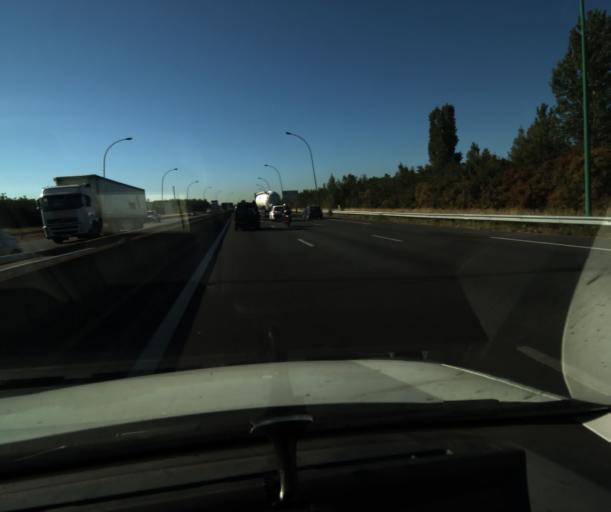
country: FR
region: Midi-Pyrenees
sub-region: Departement de la Haute-Garonne
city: Balma
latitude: 43.5835
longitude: 1.4971
